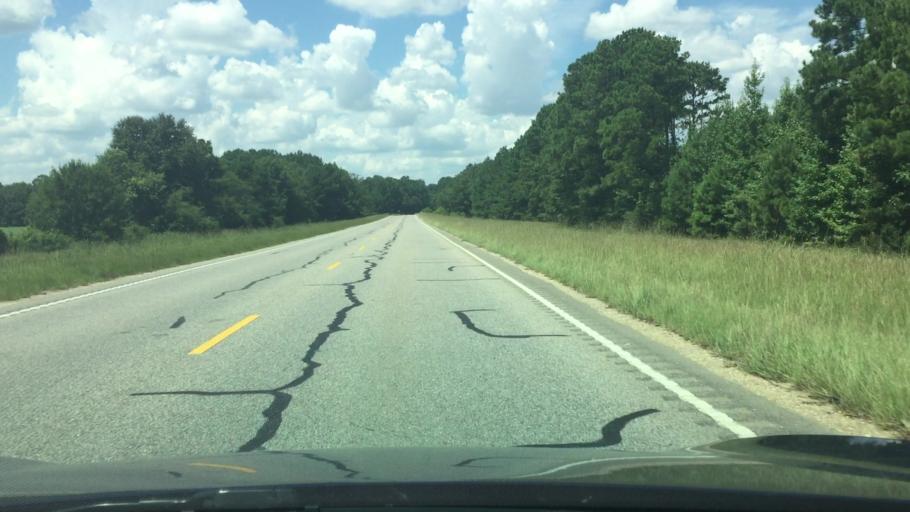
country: US
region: Alabama
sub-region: Montgomery County
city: Pike Road
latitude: 32.3717
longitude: -86.0095
